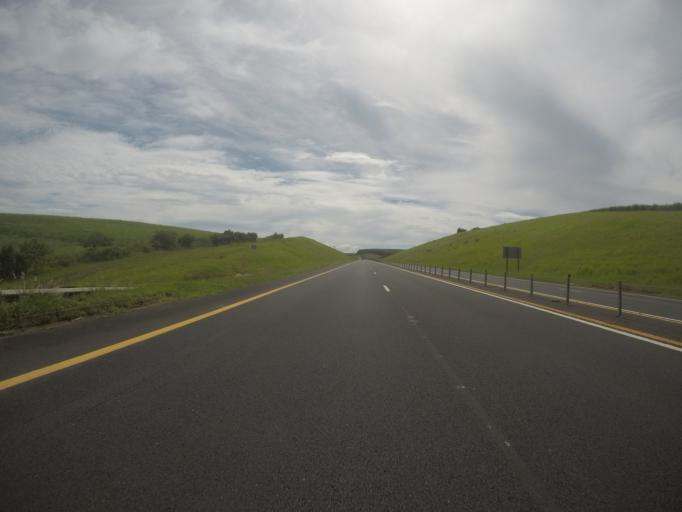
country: ZA
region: KwaZulu-Natal
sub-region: uThungulu District Municipality
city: Eshowe
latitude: -29.0493
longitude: 31.6392
